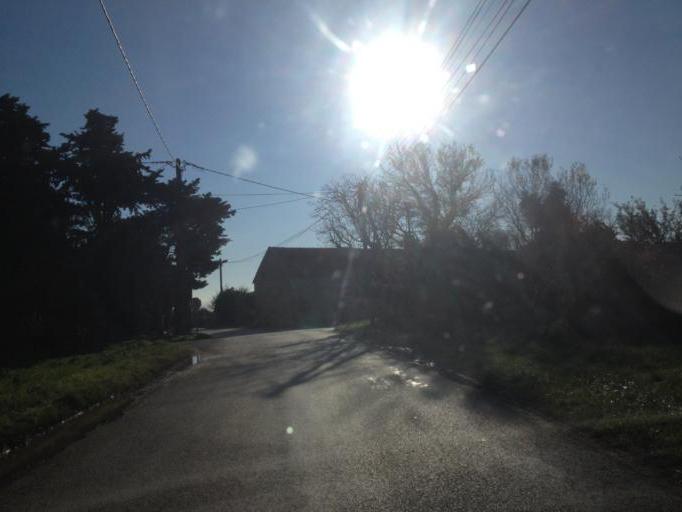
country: FR
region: Provence-Alpes-Cote d'Azur
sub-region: Departement du Vaucluse
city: Jonquieres
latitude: 44.0965
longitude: 4.9103
